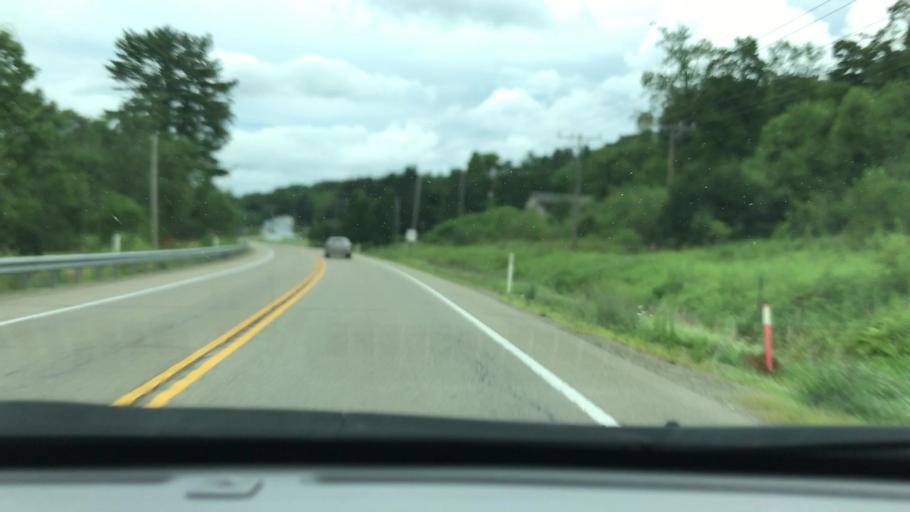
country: US
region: Pennsylvania
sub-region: Elk County
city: Johnsonburg
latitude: 41.5414
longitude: -78.6811
